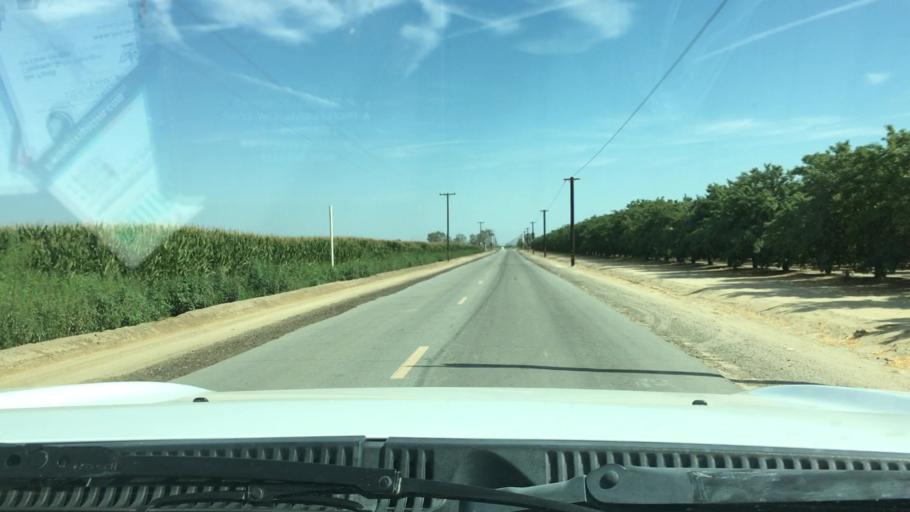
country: US
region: California
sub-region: Kern County
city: Buttonwillow
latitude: 35.4235
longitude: -119.3763
